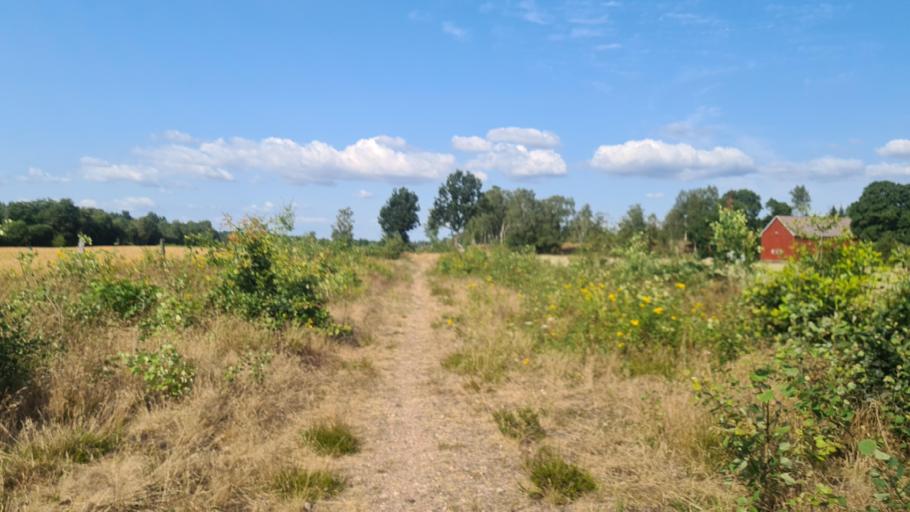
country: SE
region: Kronoberg
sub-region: Ljungby Kommun
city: Ljungby
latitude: 56.7467
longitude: 13.8800
